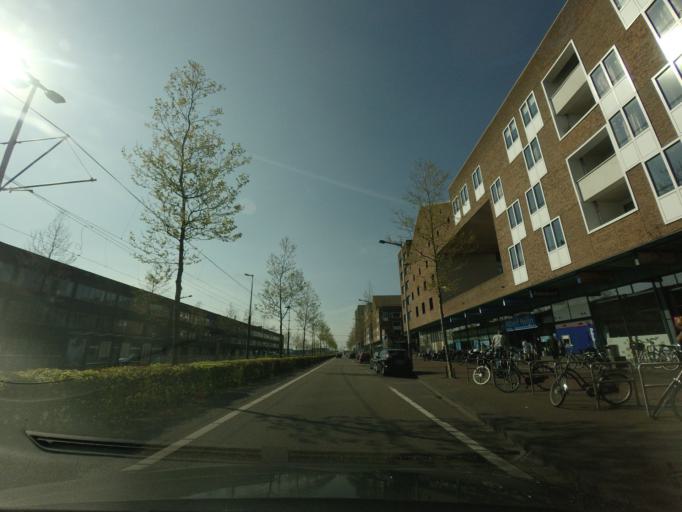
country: NL
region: North Holland
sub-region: Gemeente Diemen
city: Diemen
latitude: 52.3577
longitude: 4.9908
